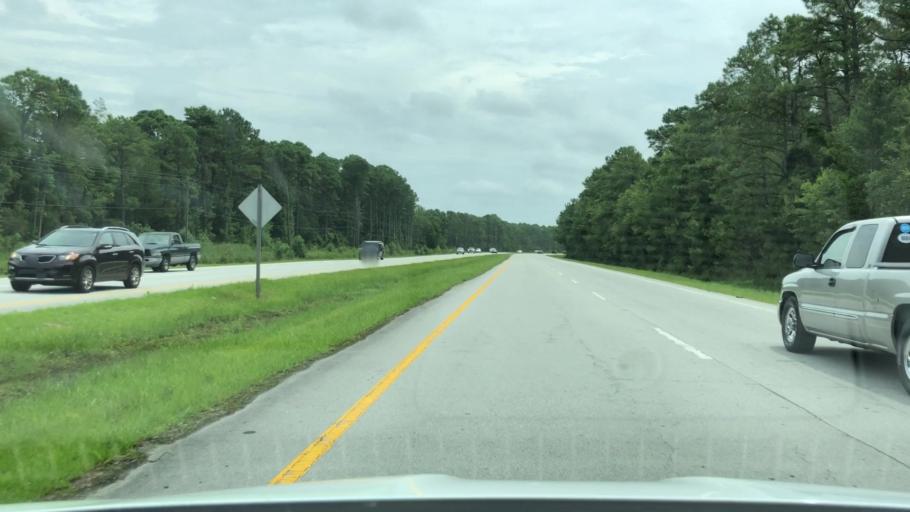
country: US
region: North Carolina
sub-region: Craven County
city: Havelock
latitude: 34.8529
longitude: -76.8913
